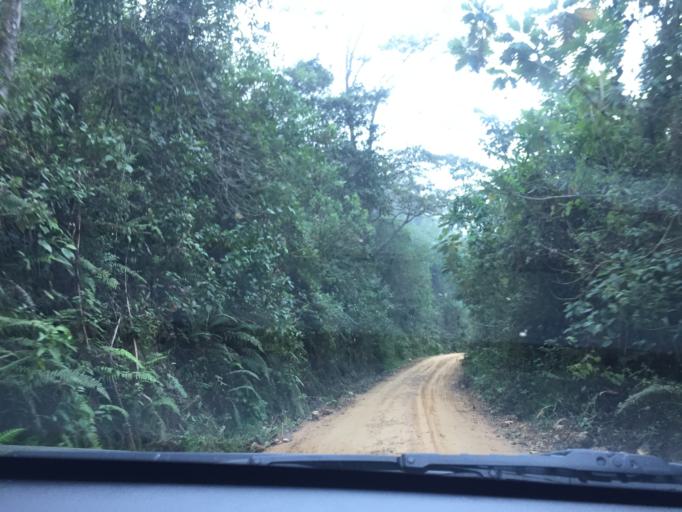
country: CO
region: Cundinamarca
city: Bojaca
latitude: 4.7039
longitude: -74.3650
